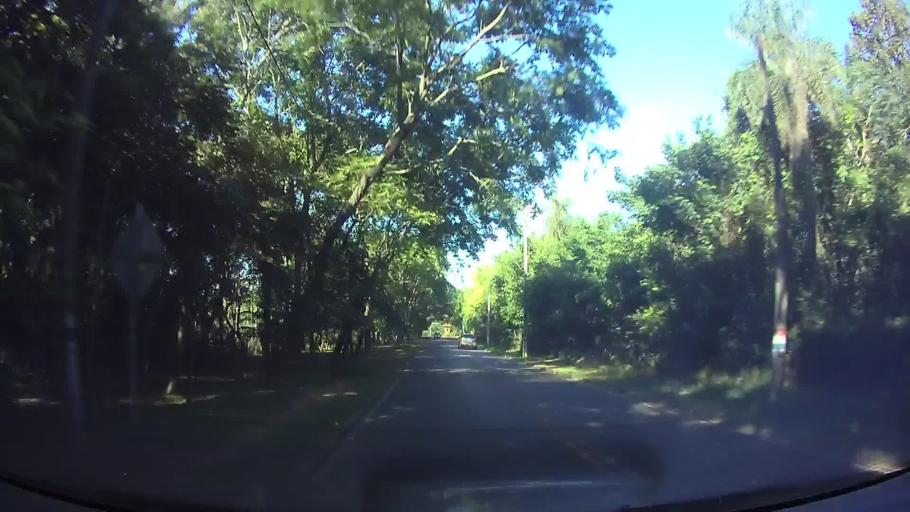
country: PY
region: Cordillera
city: Atyra
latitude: -25.2899
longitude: -57.1805
